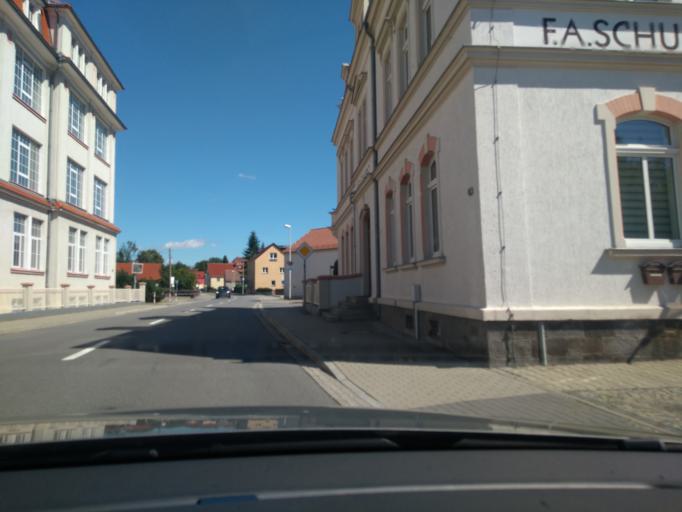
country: DE
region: Saxony
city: Grossrohrsdorf
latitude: 51.1415
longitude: 14.0119
